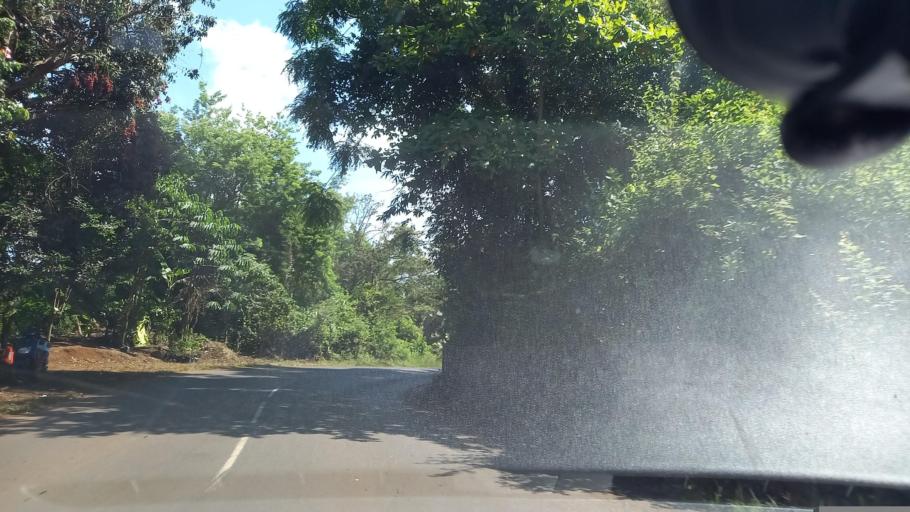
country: YT
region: Ouangani
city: Ouangani
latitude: -12.8368
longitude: 45.1435
